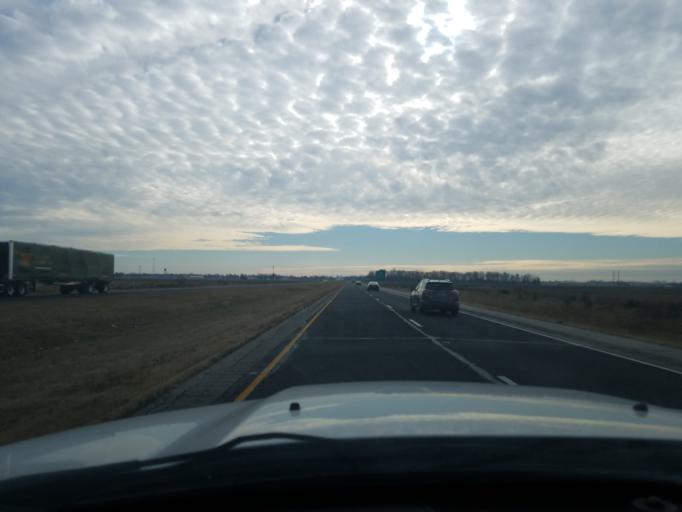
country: US
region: Indiana
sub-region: Huntington County
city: Markle
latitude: 40.8483
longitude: -85.3450
